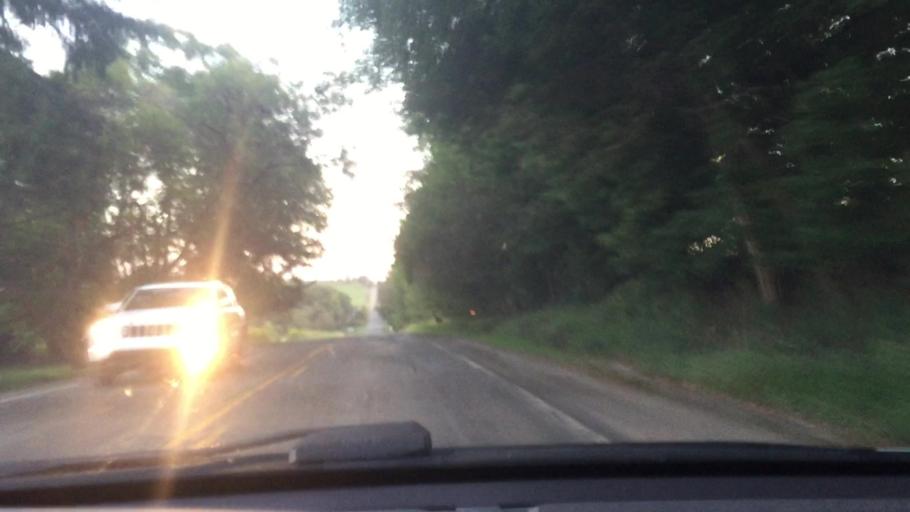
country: US
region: Pennsylvania
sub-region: Butler County
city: Slippery Rock
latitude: 41.0984
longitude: -80.0517
